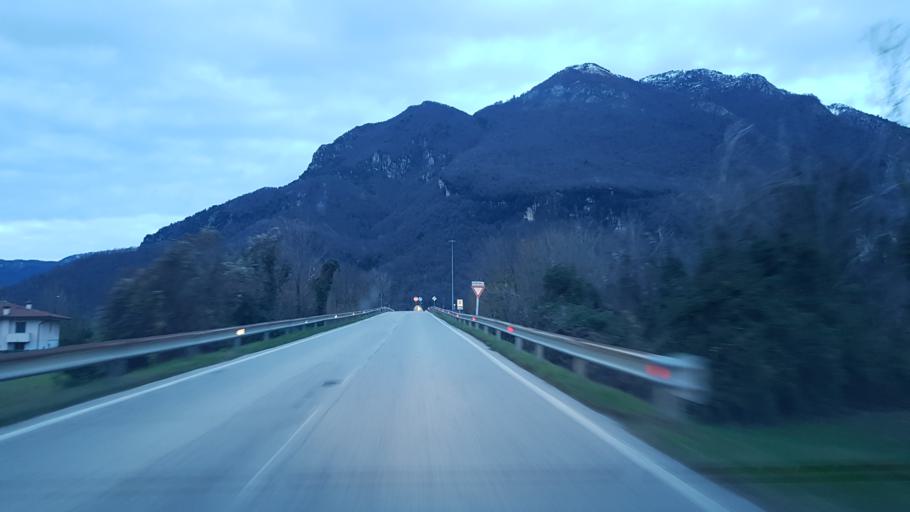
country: IT
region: Friuli Venezia Giulia
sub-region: Provincia di Udine
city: Trasaghis
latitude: 46.2801
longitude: 13.0975
